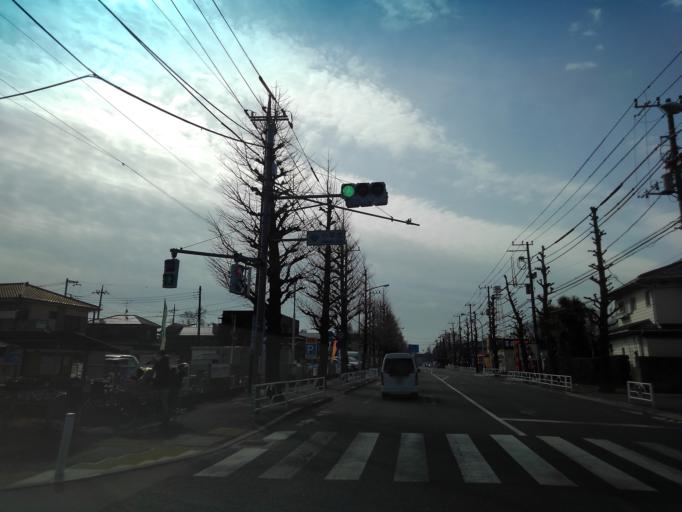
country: JP
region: Tokyo
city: Tanashicho
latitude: 35.7435
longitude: 139.5027
